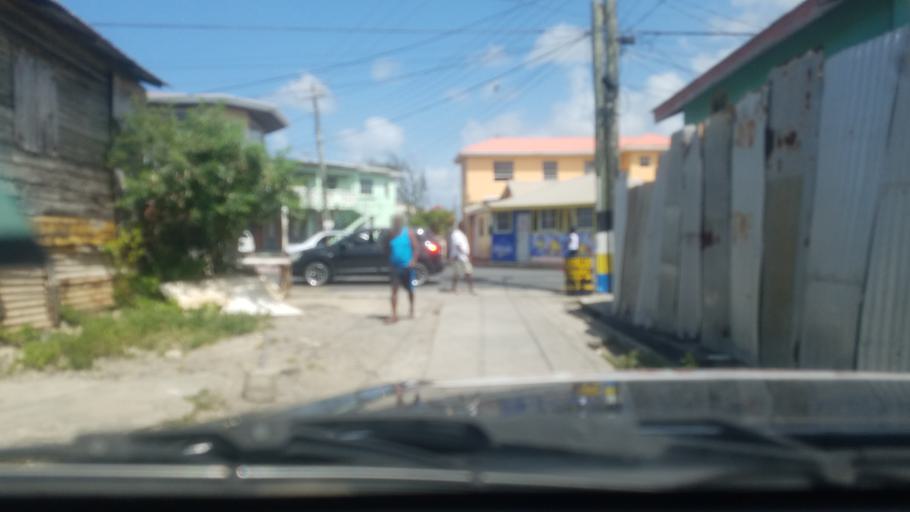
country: LC
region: Vieux-Fort
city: Vieux Fort
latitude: 13.7289
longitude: -60.9532
